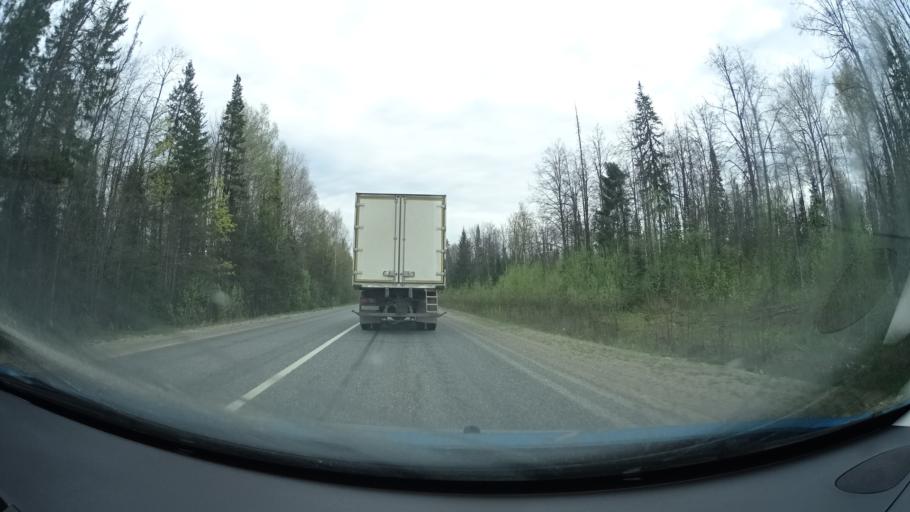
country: RU
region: Perm
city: Yugo-Kamskiy
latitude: 57.5972
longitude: 55.6553
